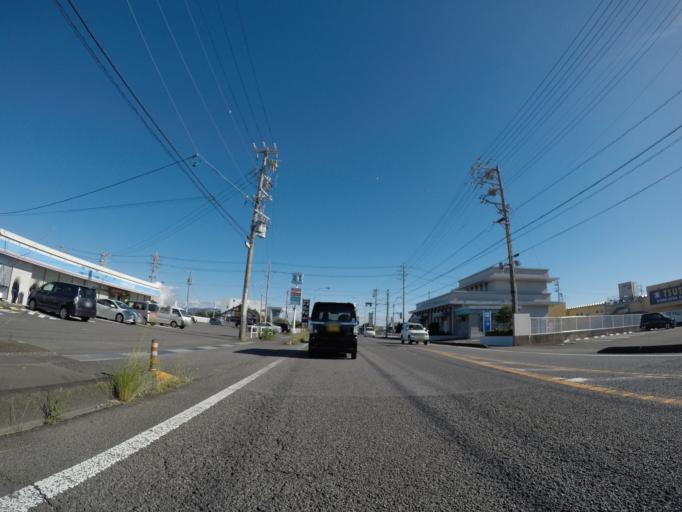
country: JP
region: Shizuoka
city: Fujieda
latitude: 34.8109
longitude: 138.2731
